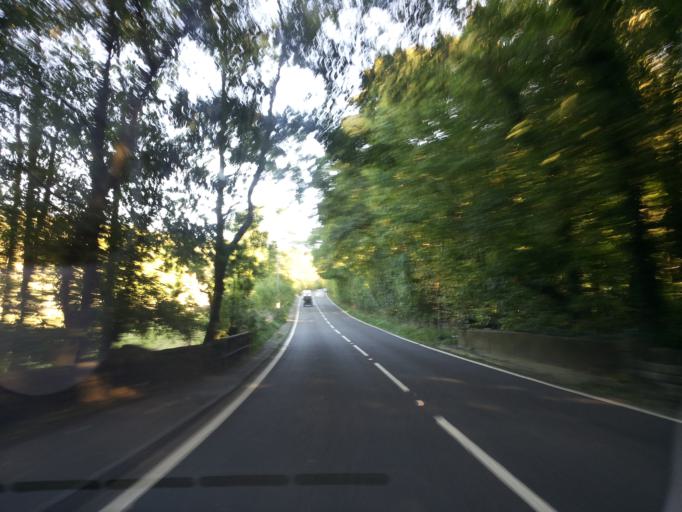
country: GB
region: England
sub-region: Derbyshire
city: Bakewell
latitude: 53.2471
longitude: -1.6041
